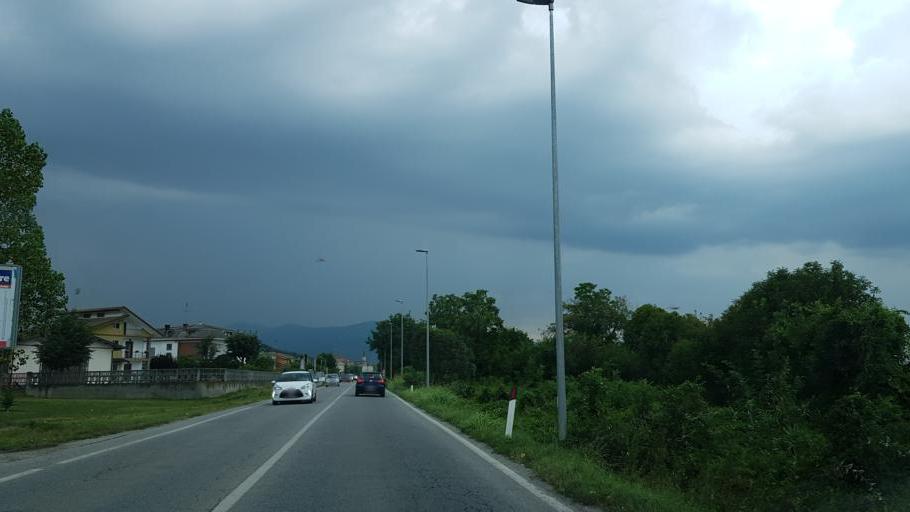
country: IT
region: Piedmont
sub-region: Provincia di Cuneo
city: Caraglio
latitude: 44.4099
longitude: 7.4408
